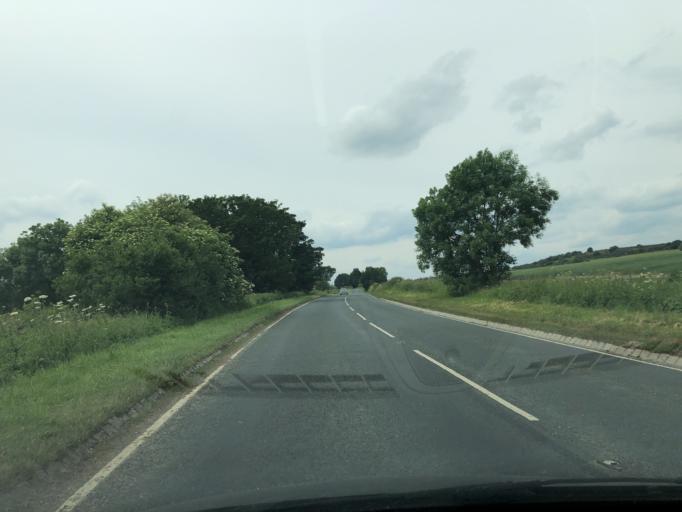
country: GB
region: England
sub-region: North Yorkshire
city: Great Habton
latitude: 54.2611
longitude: -0.8775
